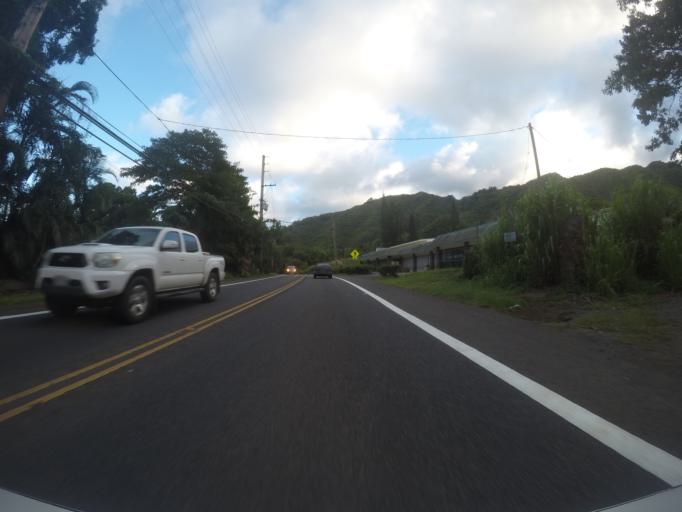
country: US
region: Hawaii
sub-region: Honolulu County
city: Ka'a'awa
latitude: 21.5073
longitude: -157.8558
